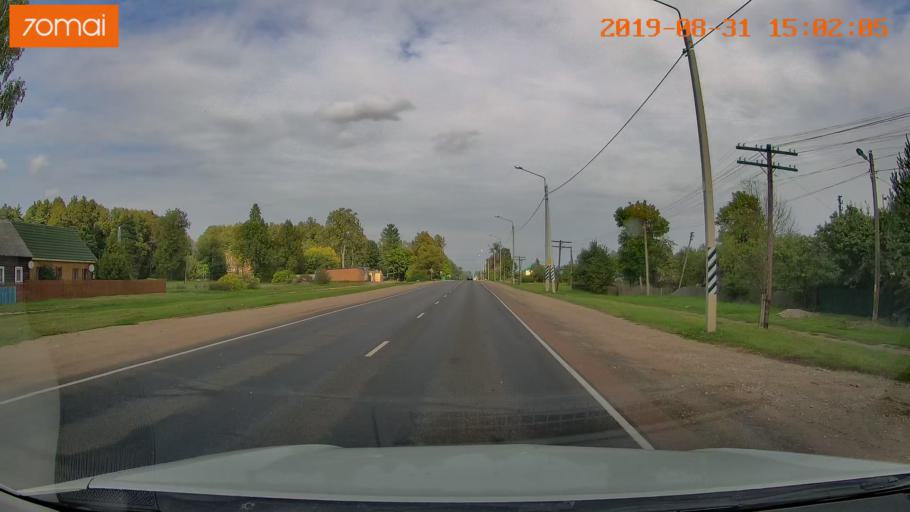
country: RU
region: Kaluga
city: Spas-Demensk
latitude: 54.3433
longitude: 34.0686
